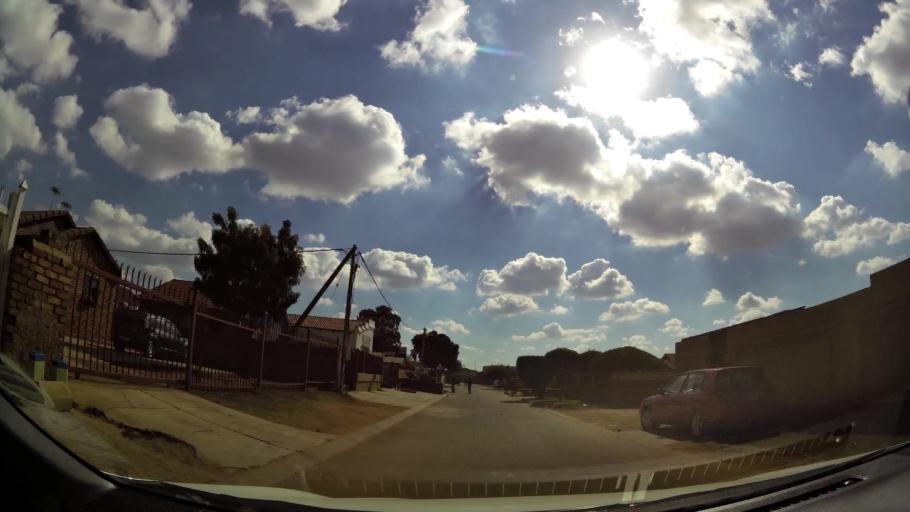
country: ZA
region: Gauteng
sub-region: City of Tshwane Metropolitan Municipality
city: Cullinan
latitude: -25.7075
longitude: 28.4181
